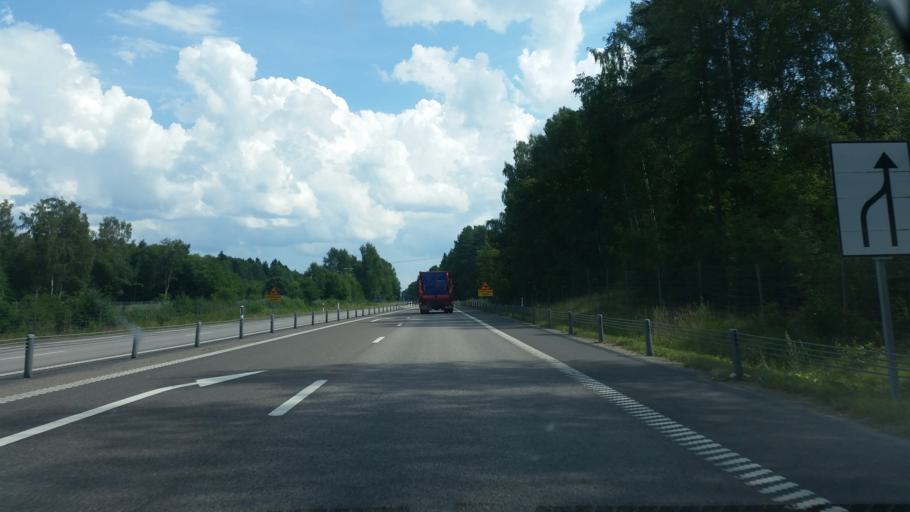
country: SE
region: Vaestra Goetaland
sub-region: Skara Kommun
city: Axvall
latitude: 58.3974
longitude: 13.5685
